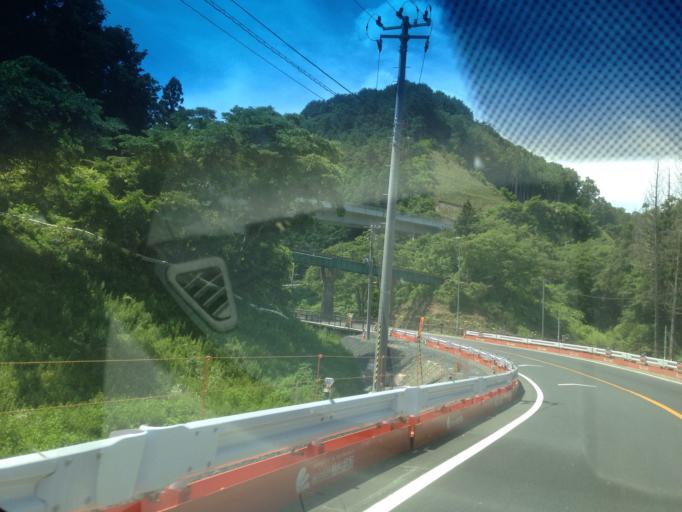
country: JP
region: Iwate
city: Kamaishi
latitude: 39.3118
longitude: 141.8859
